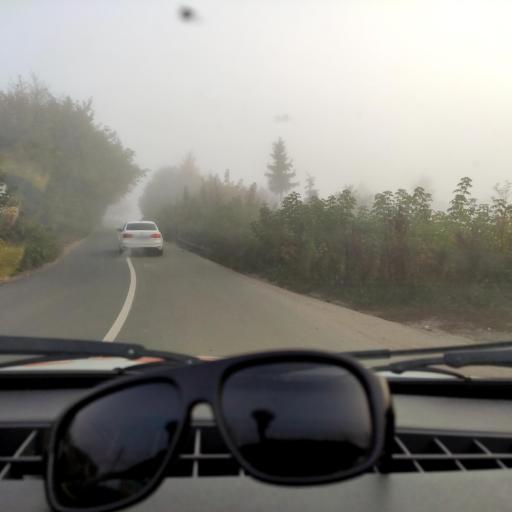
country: RU
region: Bashkortostan
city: Ufa
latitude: 54.7154
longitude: 55.9691
